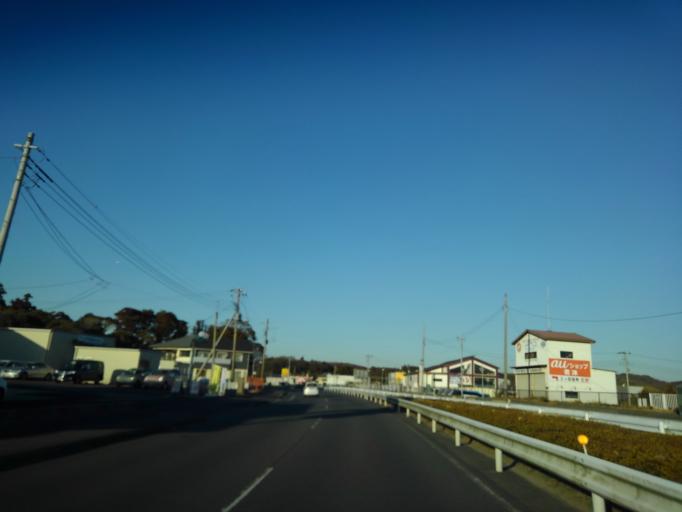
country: JP
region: Chiba
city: Kimitsu
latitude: 35.3133
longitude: 139.9265
